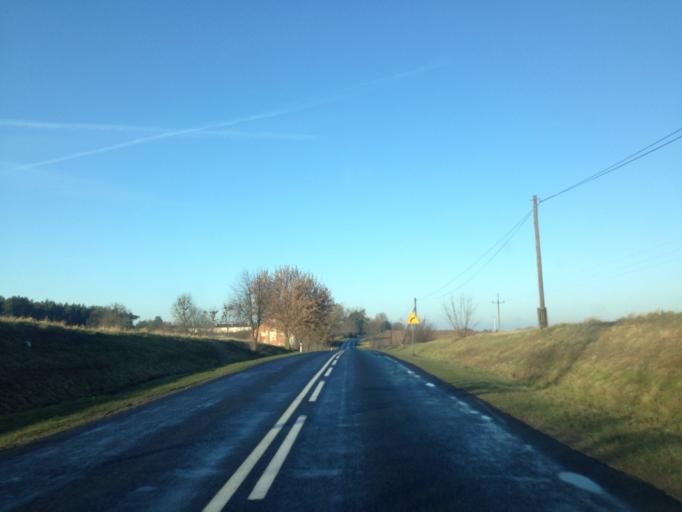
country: PL
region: Kujawsko-Pomorskie
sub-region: Powiat brodnicki
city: Bobrowo
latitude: 53.3301
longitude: 19.2351
